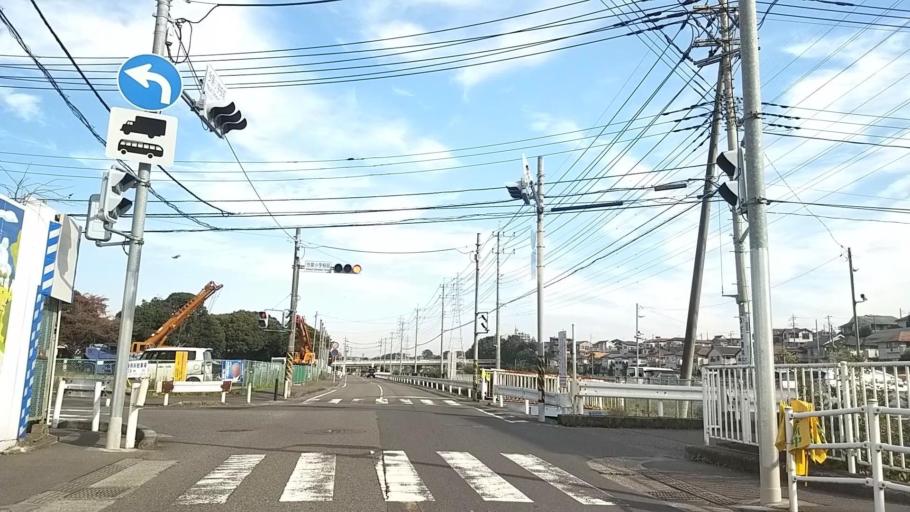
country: JP
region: Kanagawa
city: Zama
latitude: 35.4600
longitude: 139.3925
